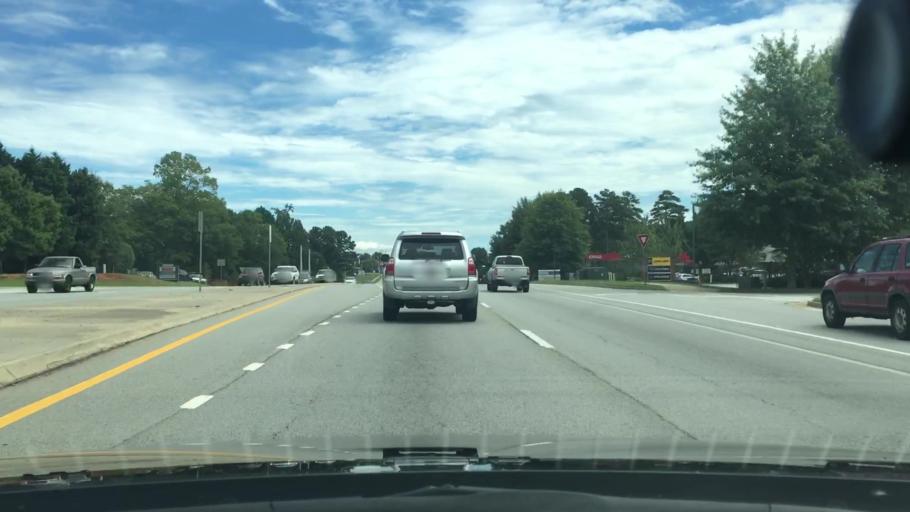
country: US
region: Georgia
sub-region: Coweta County
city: Newnan
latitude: 33.3993
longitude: -84.7670
